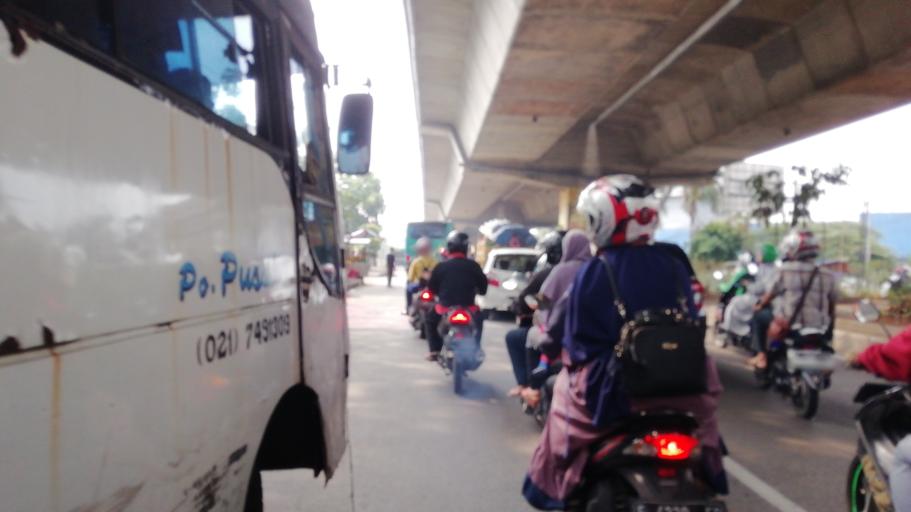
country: ID
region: West Java
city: Bogor
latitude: -6.5638
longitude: 106.8101
